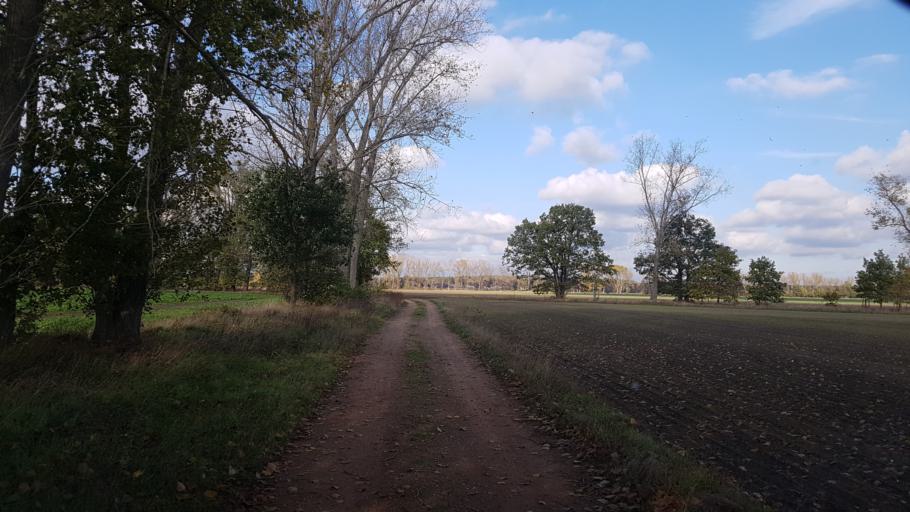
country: DE
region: Brandenburg
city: Schonewalde
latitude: 51.6886
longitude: 13.5766
